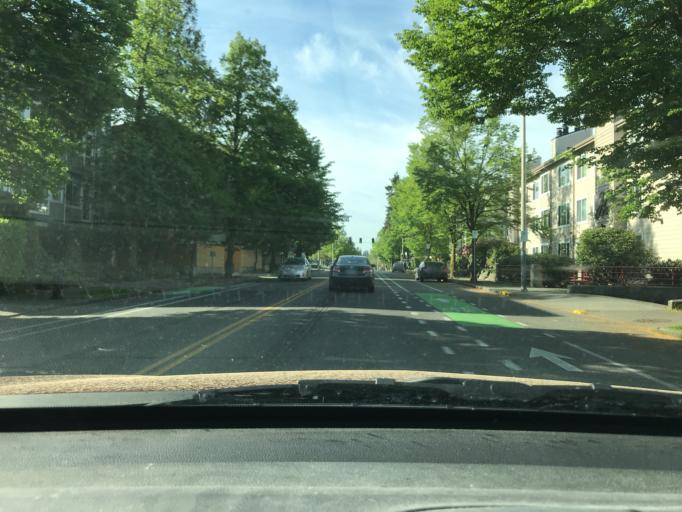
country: US
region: Washington
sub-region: King County
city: Shoreline
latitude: 47.7171
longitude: -122.3126
